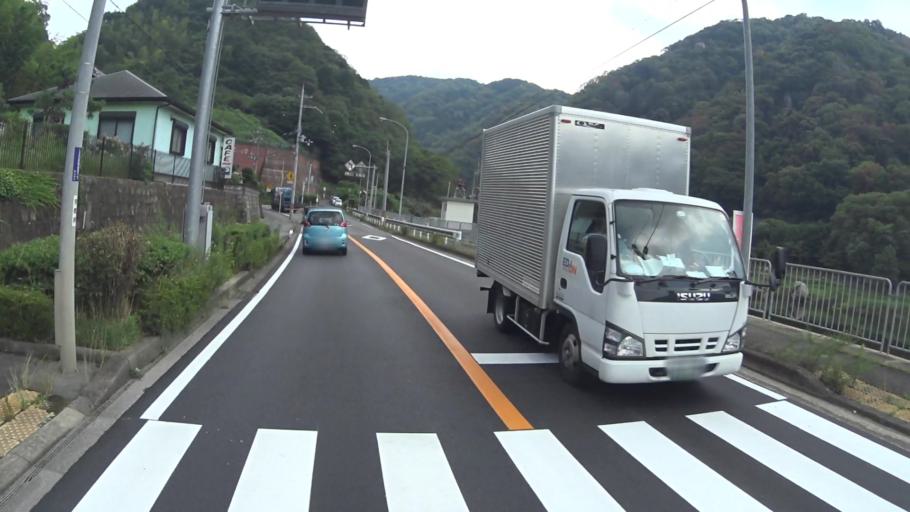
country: JP
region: Nara
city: Nara-shi
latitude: 34.7598
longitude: 135.9399
